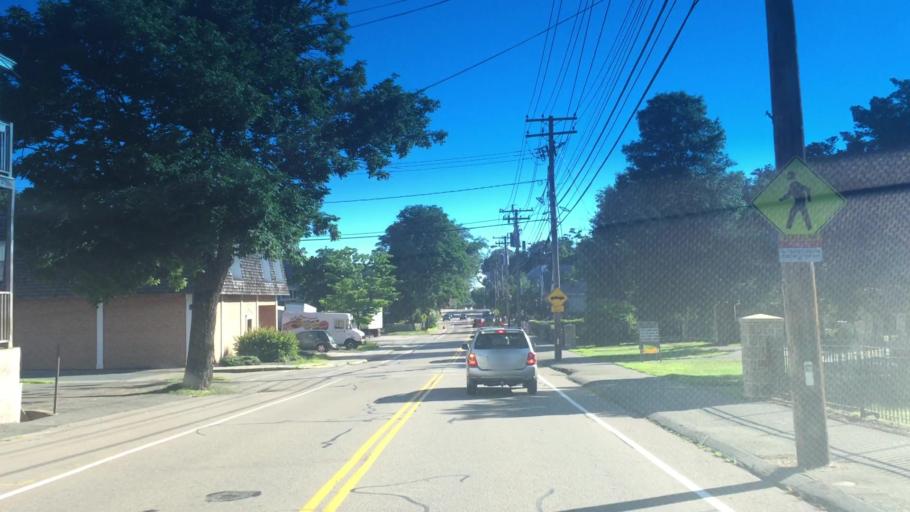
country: US
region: Massachusetts
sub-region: Norfolk County
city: Walpole
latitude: 42.1581
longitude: -71.2192
